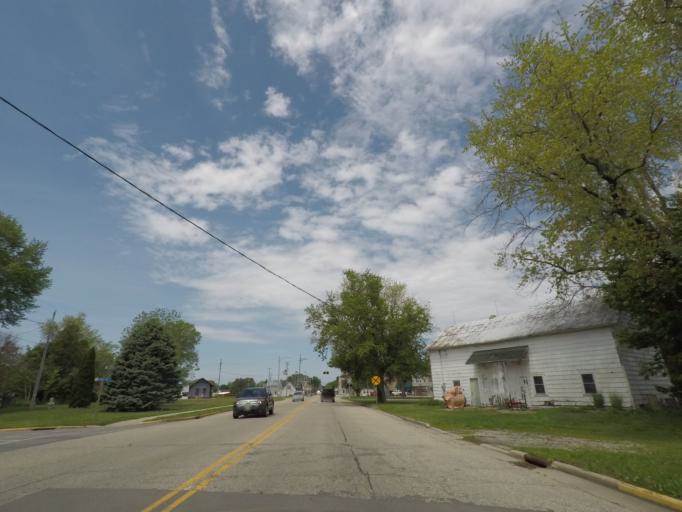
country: US
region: Wisconsin
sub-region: Rock County
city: Orfordville
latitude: 42.6275
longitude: -89.2545
